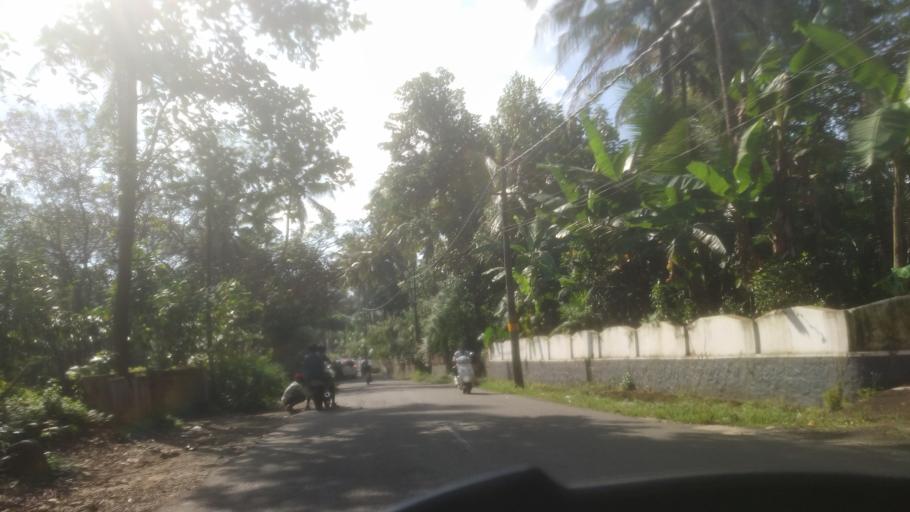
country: IN
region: Kerala
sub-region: Ernakulam
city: Muvattupula
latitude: 9.9981
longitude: 76.6246
